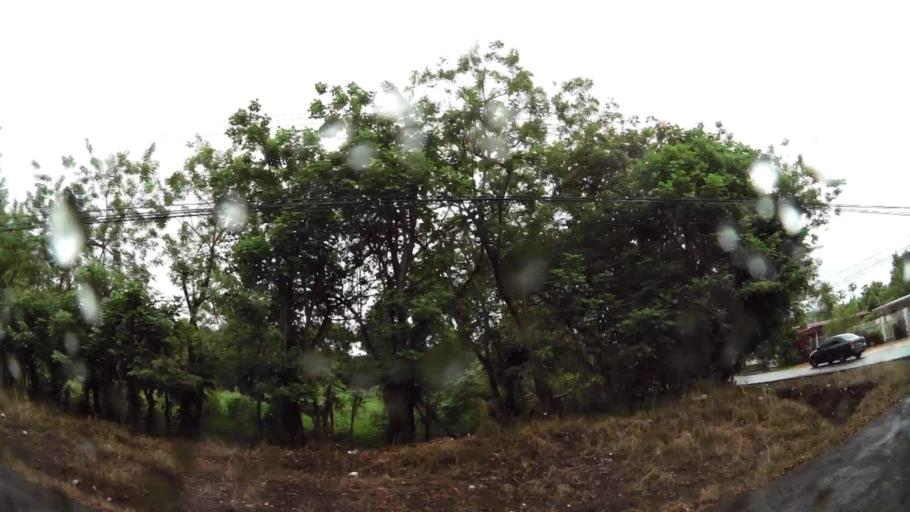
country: PA
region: Chiriqui
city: David
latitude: 8.4303
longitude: -82.4372
